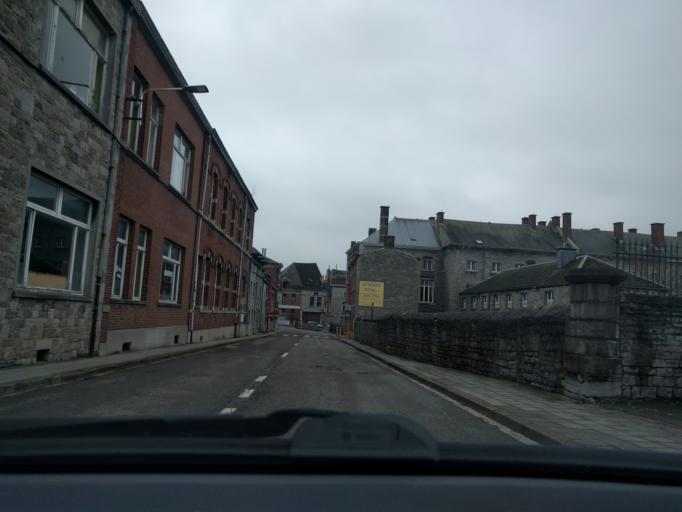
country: BE
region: Wallonia
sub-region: Province de Namur
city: Couvin
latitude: 50.0535
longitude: 4.4967
